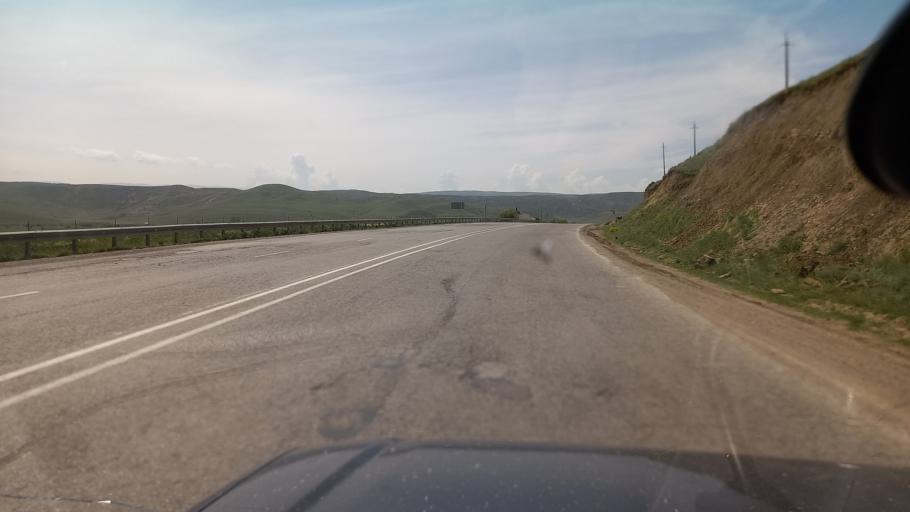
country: RU
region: Dagestan
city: Karabudakhkent
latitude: 42.7020
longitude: 47.6200
